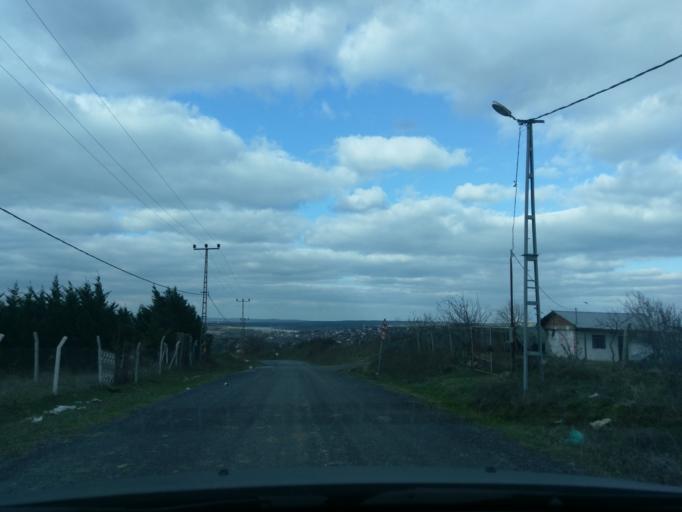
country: TR
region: Istanbul
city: Durusu
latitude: 41.2854
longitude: 28.6942
